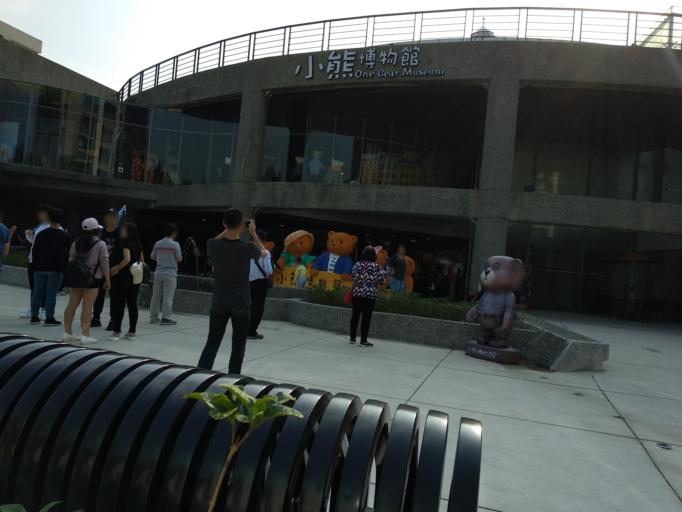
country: TW
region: Taiwan
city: Daxi
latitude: 24.7889
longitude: 121.1839
